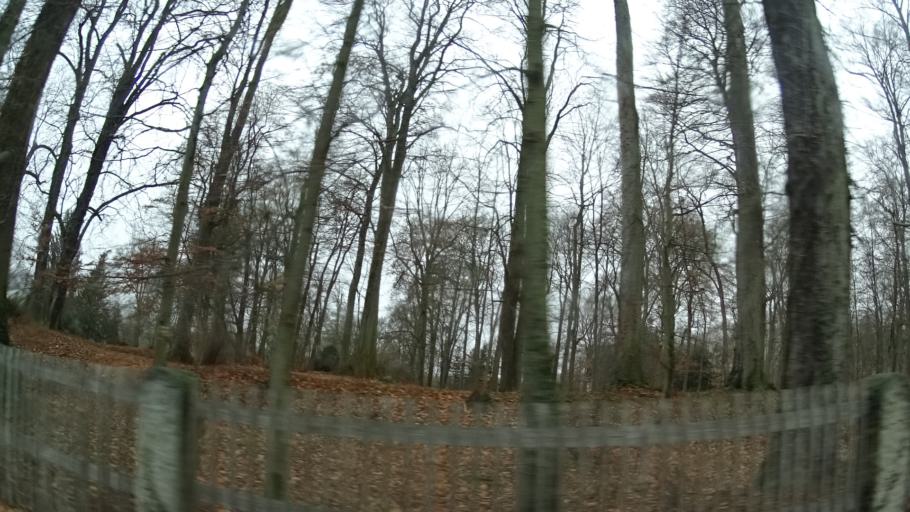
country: DE
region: Thuringia
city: Rudolstadt
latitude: 50.7777
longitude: 11.3581
